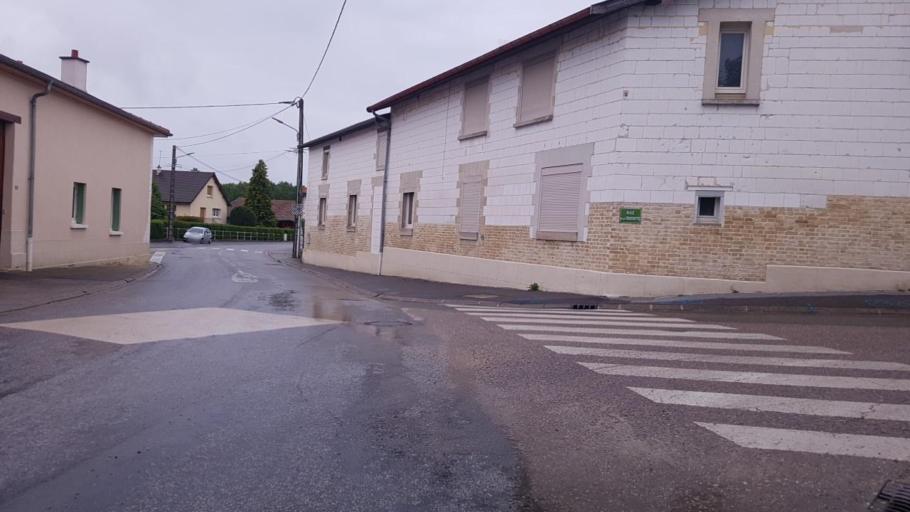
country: FR
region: Champagne-Ardenne
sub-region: Departement de la Marne
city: Sarry
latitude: 48.9088
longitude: 4.4268
